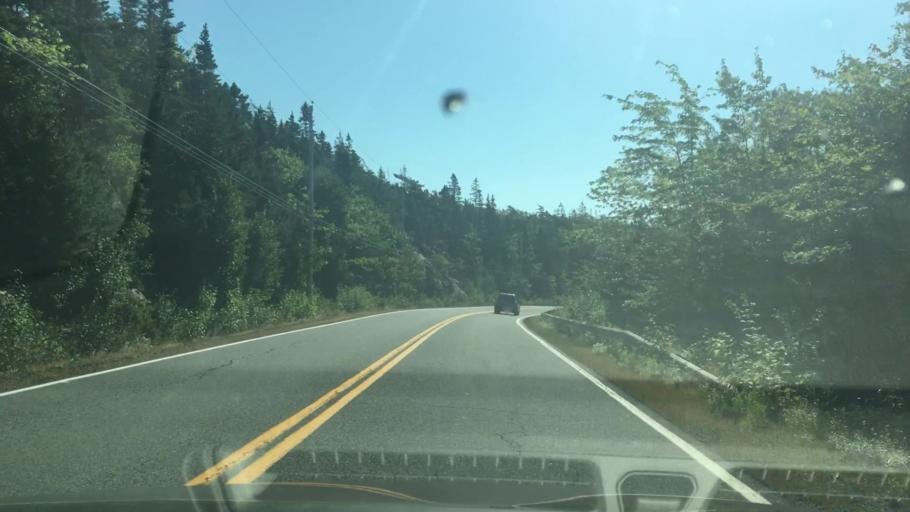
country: CA
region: Nova Scotia
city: Cole Harbour
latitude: 44.8120
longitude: -62.8380
